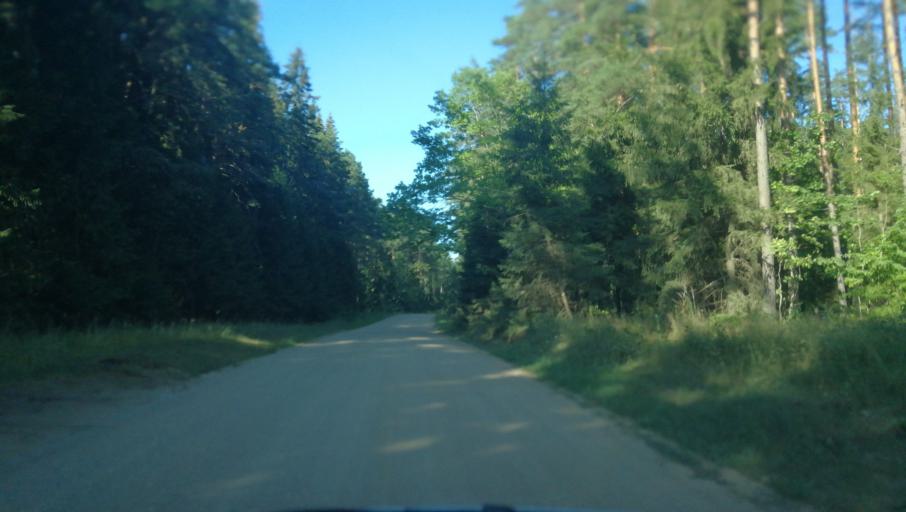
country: LV
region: Cesu Rajons
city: Cesis
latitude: 57.2766
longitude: 25.2003
